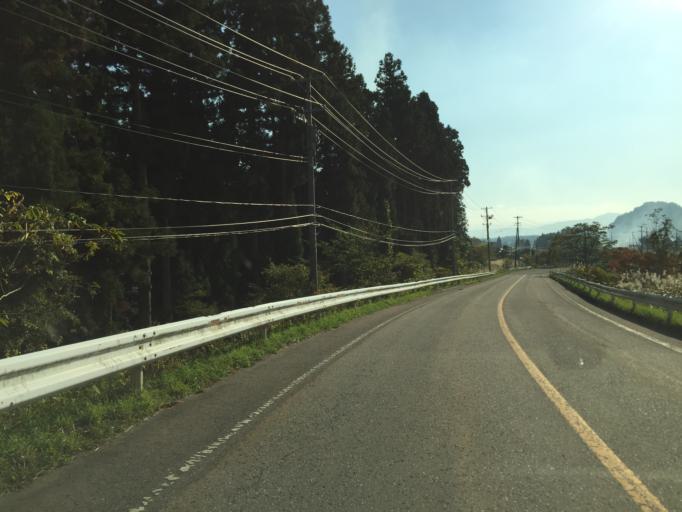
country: JP
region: Fukushima
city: Kitakata
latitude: 37.7462
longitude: 139.8953
